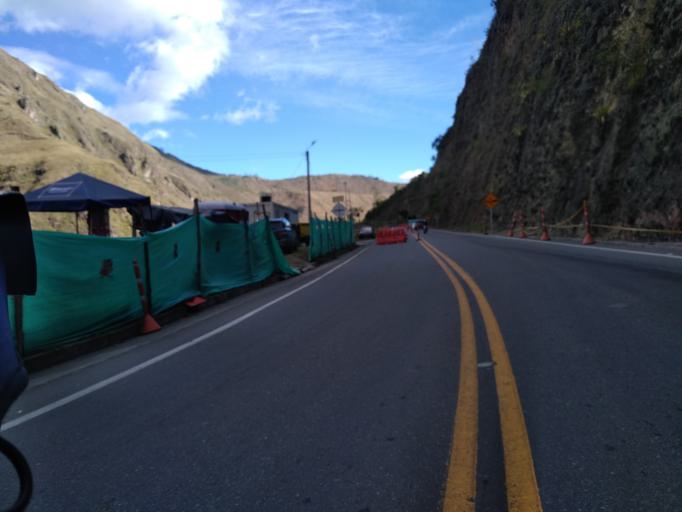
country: CO
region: Narino
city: Imues
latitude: 1.0567
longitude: -77.4492
